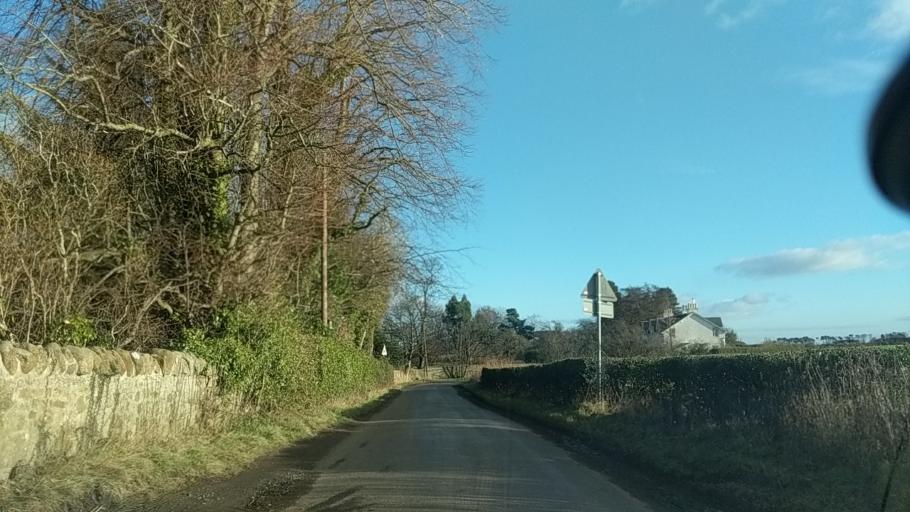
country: GB
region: Scotland
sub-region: West Lothian
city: Broxburn
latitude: 55.9735
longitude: -3.4472
